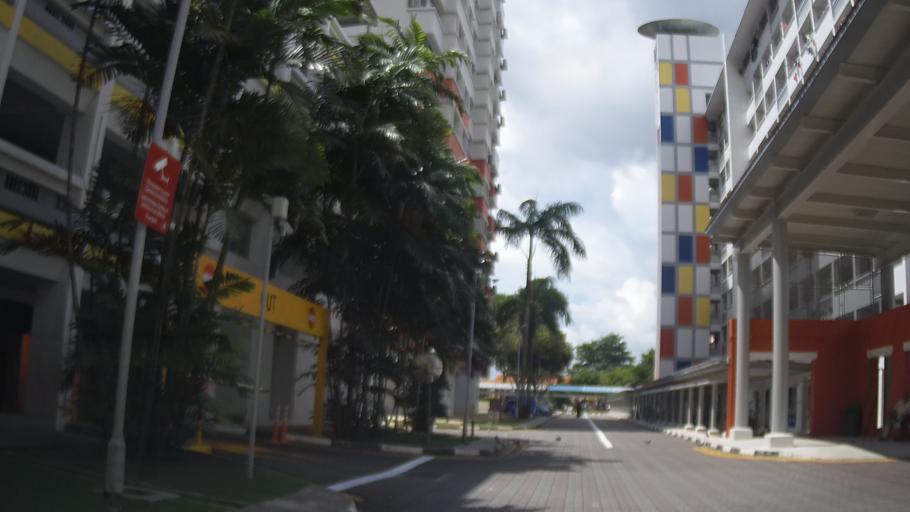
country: SG
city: Singapore
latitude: 1.3306
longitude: 103.8871
